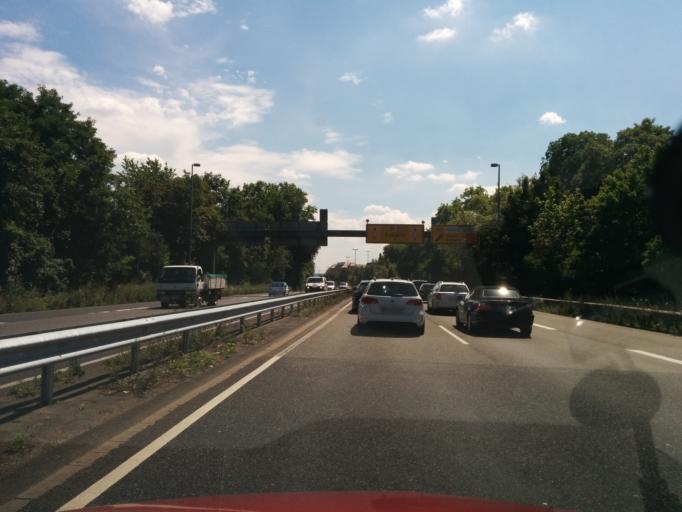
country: DE
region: Rheinland-Pfalz
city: Koblenz
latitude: 50.3730
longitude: 7.5867
